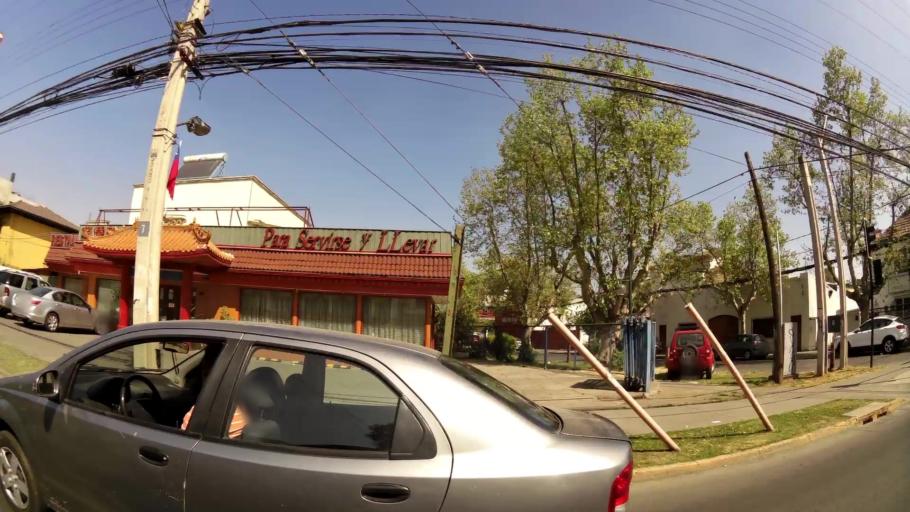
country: CL
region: Santiago Metropolitan
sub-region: Provincia de Santiago
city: Santiago
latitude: -33.4552
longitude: -70.6247
